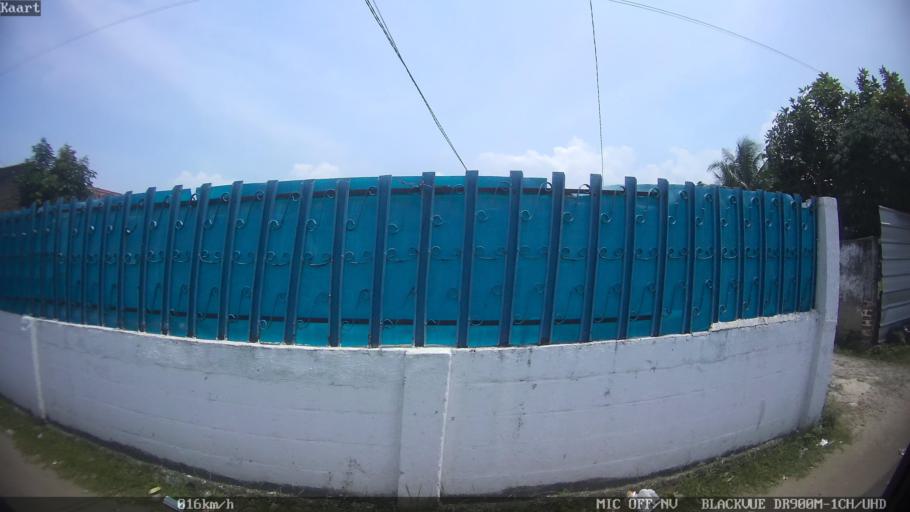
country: ID
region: Lampung
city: Bandarlampung
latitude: -5.4470
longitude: 105.2559
